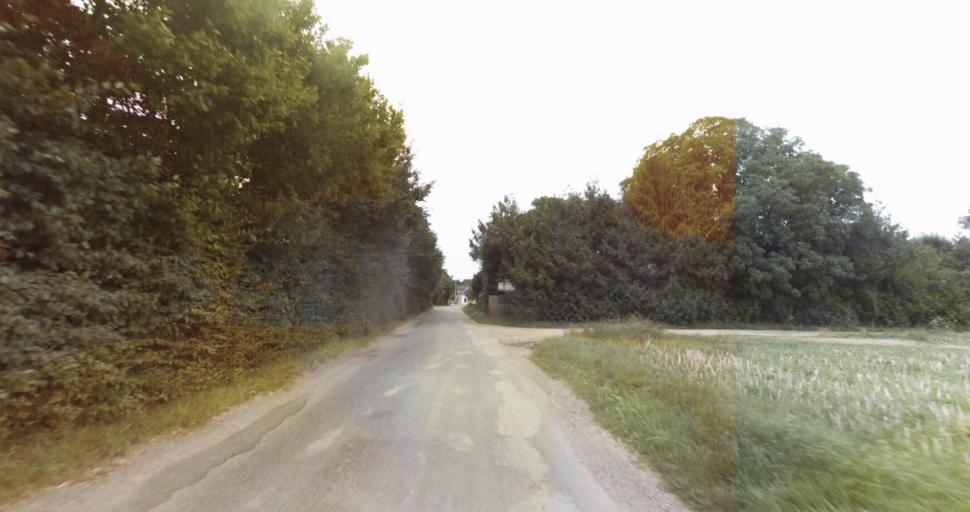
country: FR
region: Haute-Normandie
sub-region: Departement de l'Eure
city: Saint-Germain-sur-Avre
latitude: 48.8183
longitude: 1.2883
